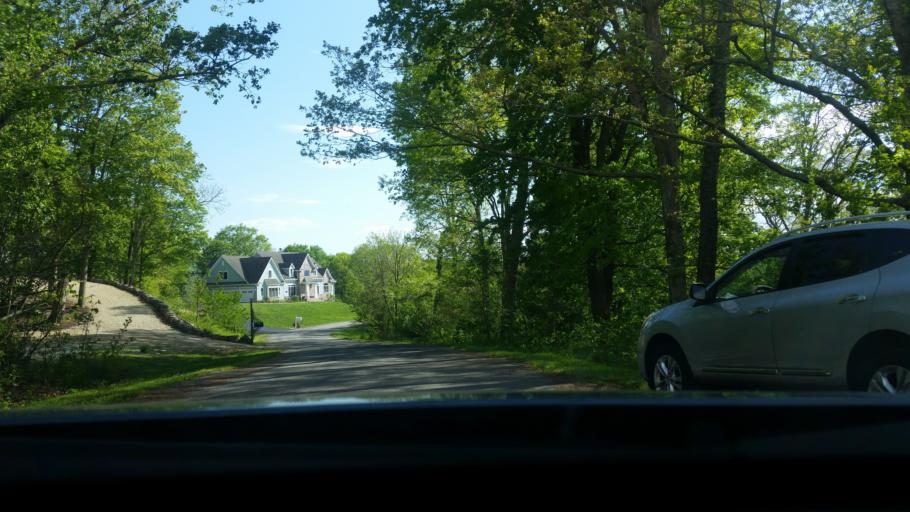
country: US
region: Virginia
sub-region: Giles County
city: Pembroke
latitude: 37.3122
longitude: -80.6263
